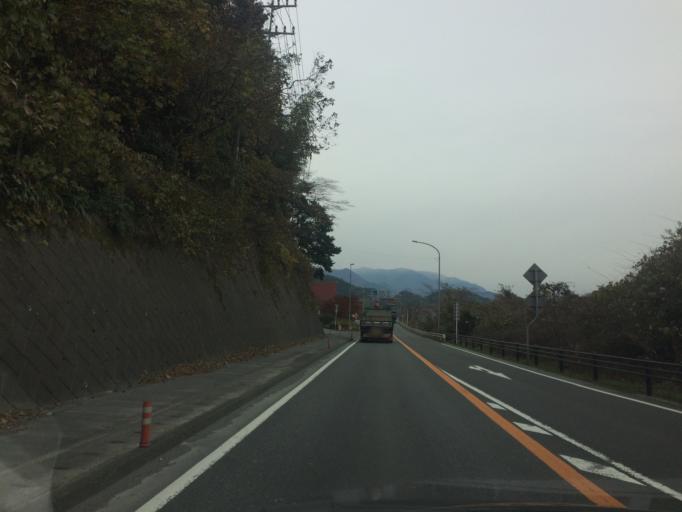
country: JP
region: Shizuoka
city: Fujinomiya
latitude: 35.2387
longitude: 138.4894
